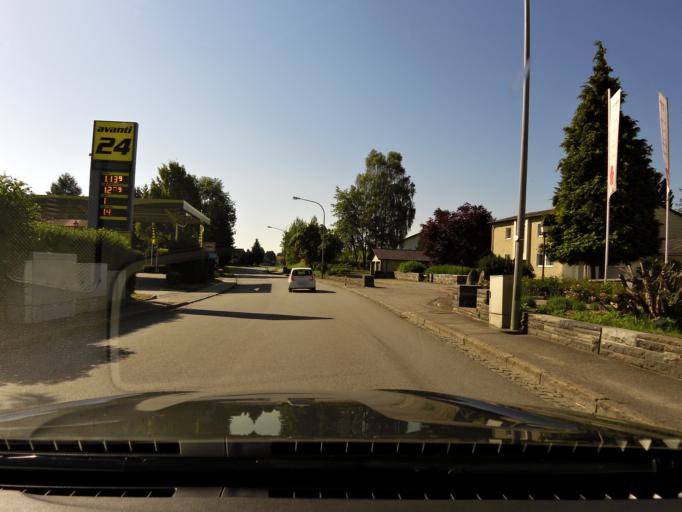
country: DE
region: Bavaria
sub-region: Upper Bavaria
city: Egglkofen
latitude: 48.3918
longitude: 12.4525
